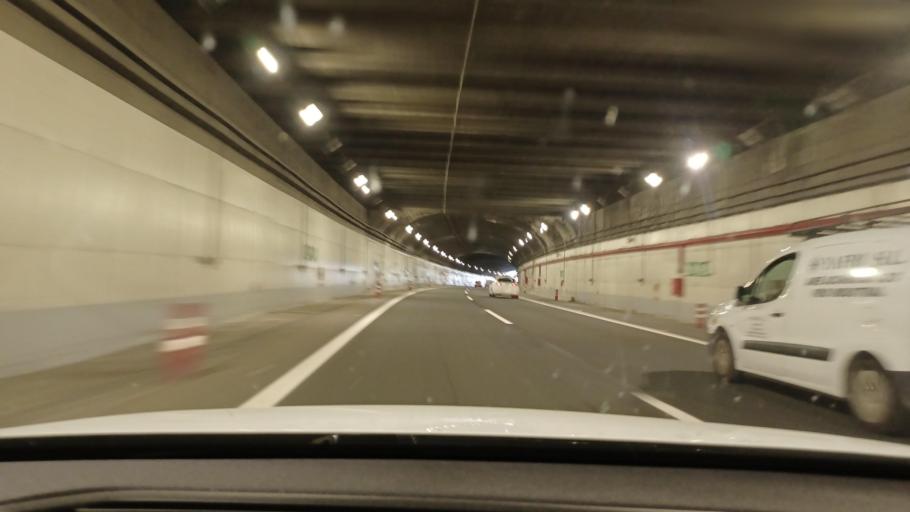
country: ES
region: Valencia
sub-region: Provincia de Alicante
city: Villena
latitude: 38.6352
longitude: -0.8583
